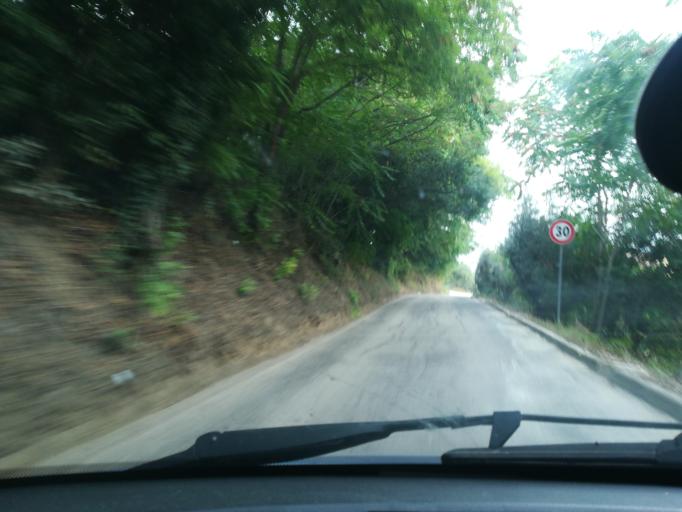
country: IT
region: The Marches
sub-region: Provincia di Macerata
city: Piediripa
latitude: 43.2943
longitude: 13.4860
